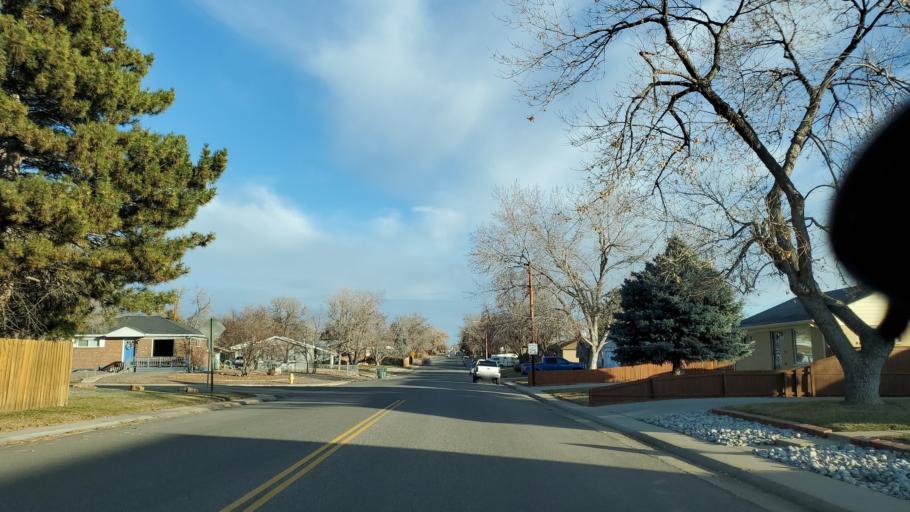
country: US
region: Colorado
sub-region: Adams County
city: Northglenn
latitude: 39.9004
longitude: -104.9615
